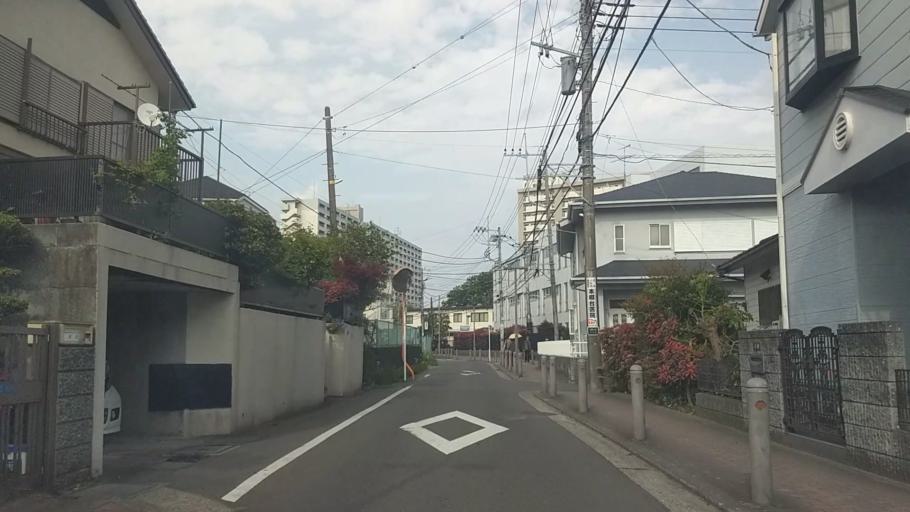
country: JP
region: Kanagawa
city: Kamakura
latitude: 35.3654
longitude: 139.5470
